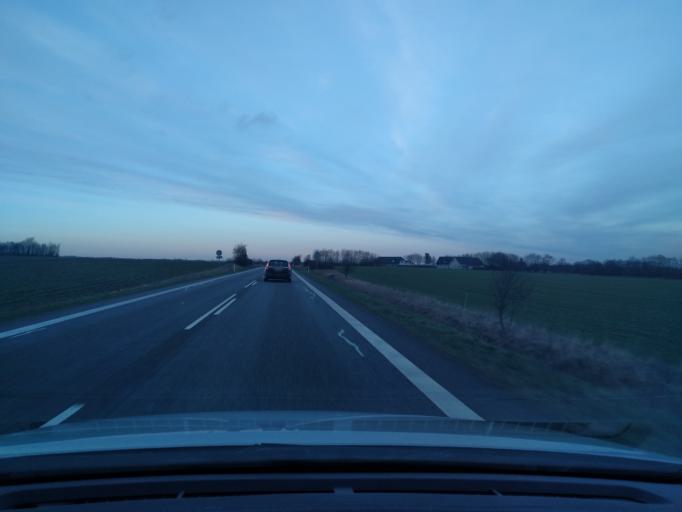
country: DK
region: South Denmark
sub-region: Tonder Kommune
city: Toftlund
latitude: 55.2115
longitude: 9.0970
